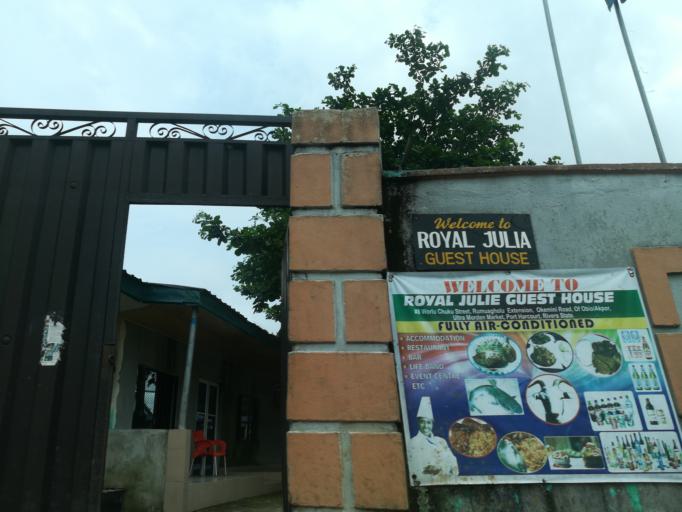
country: NG
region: Rivers
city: Port Harcourt
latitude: 4.8904
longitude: 6.9825
